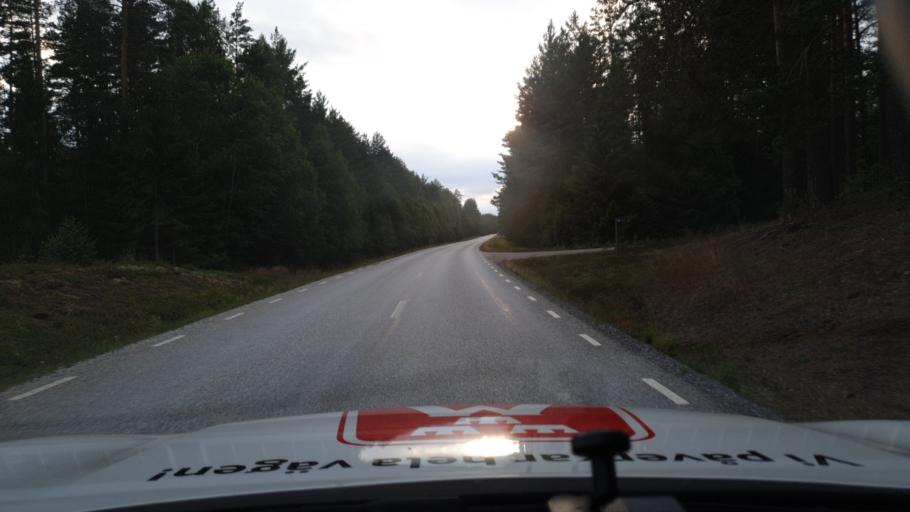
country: SE
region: Dalarna
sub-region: Smedjebackens Kommun
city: Smedjebacken
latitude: 59.9123
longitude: 15.4643
